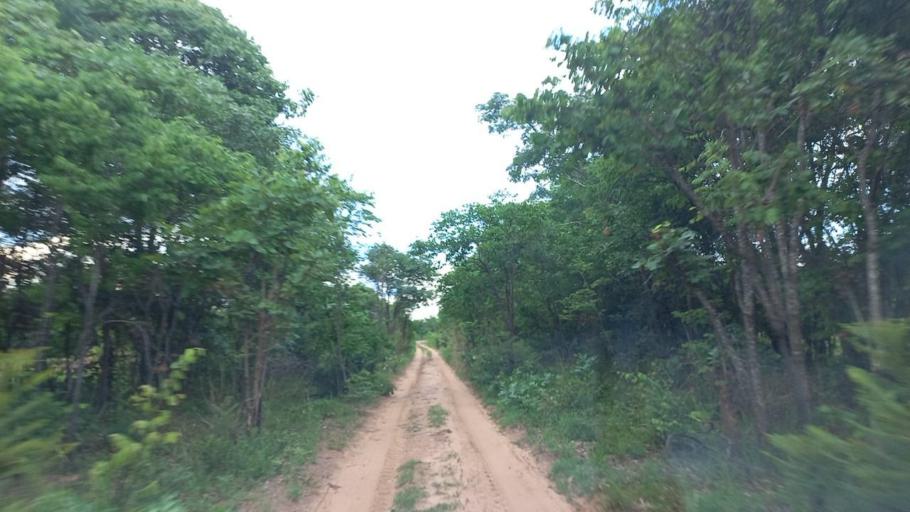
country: ZM
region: North-Western
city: Kabompo
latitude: -13.2409
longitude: 24.5350
